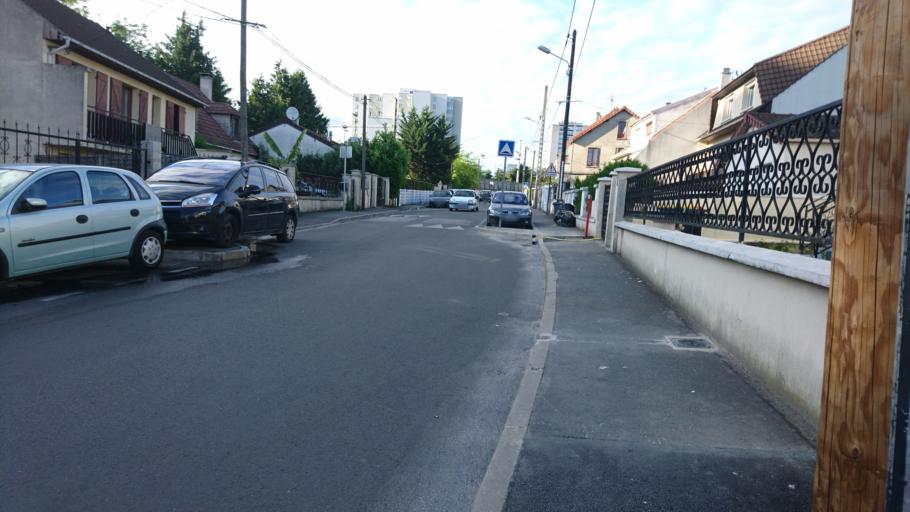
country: FR
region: Ile-de-France
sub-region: Departement du Val-d'Oise
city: Garges-les-Gonesse
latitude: 48.9721
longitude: 2.3851
